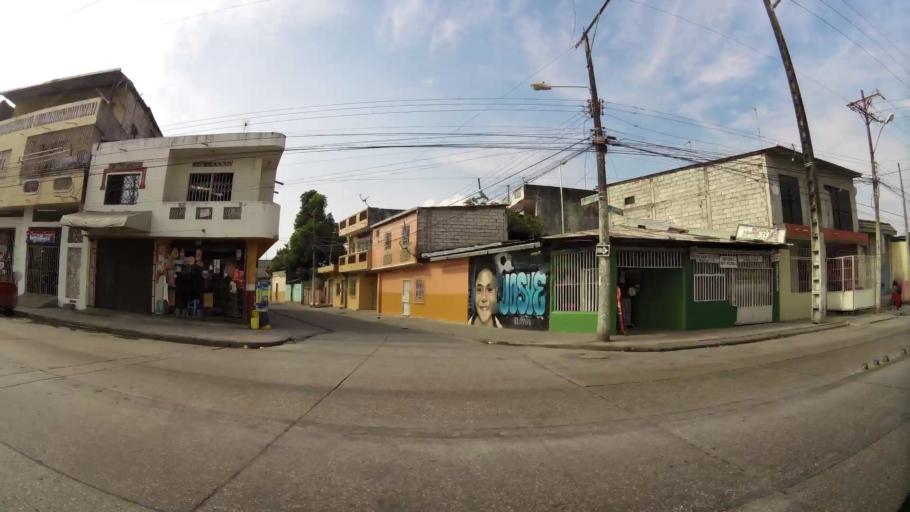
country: EC
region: Guayas
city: Guayaquil
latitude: -2.2569
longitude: -79.8976
